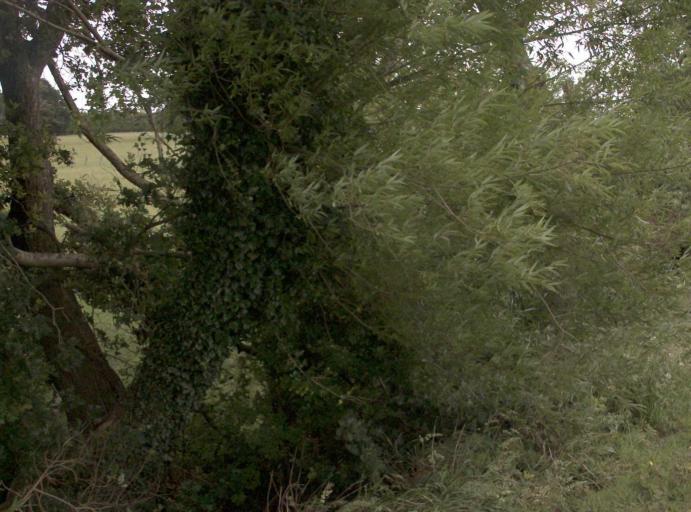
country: AU
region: Victoria
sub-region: Baw Baw
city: Warragul
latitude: -38.1688
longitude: 145.9703
